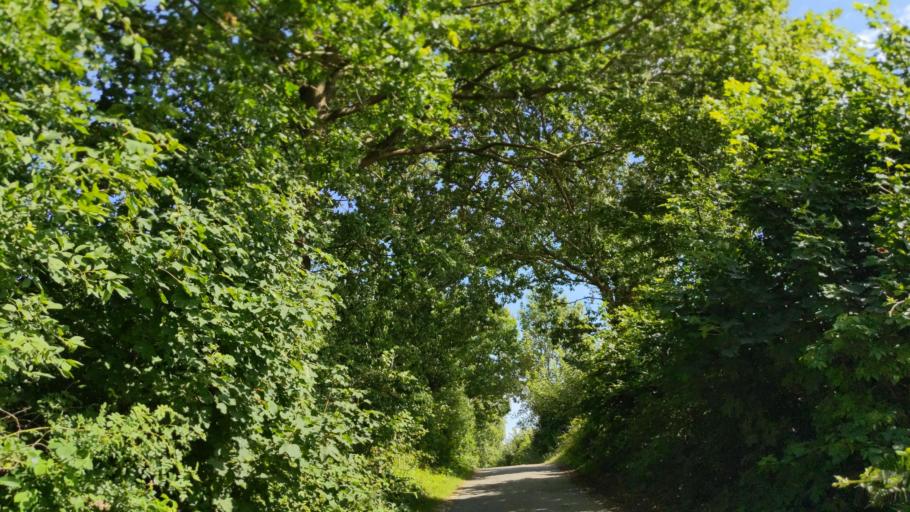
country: DE
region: Schleswig-Holstein
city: Kasseedorf
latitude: 54.1279
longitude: 10.7400
